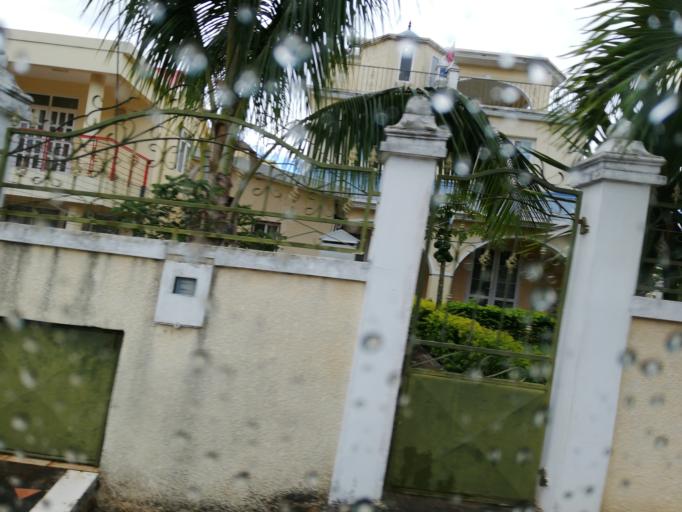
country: MU
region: Moka
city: Pailles
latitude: -20.2070
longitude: 57.4685
